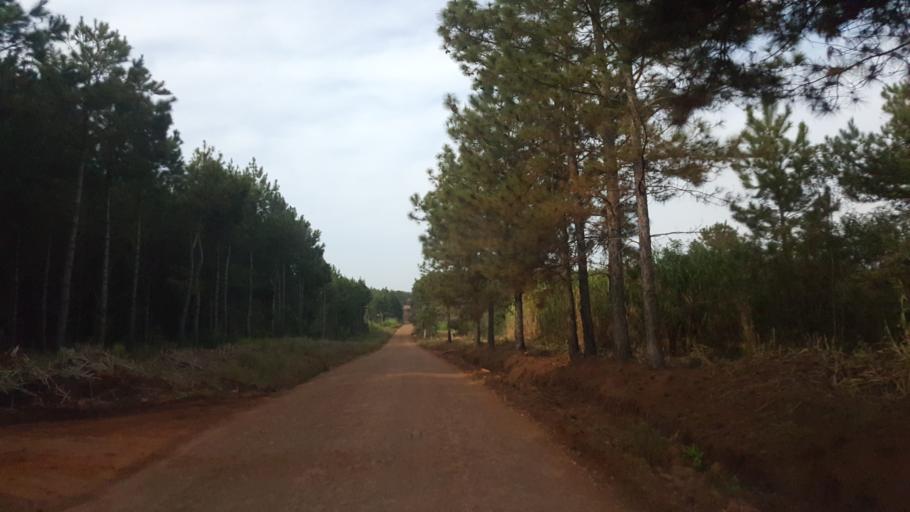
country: AR
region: Misiones
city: Capiovi
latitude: -26.9265
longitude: -55.1162
